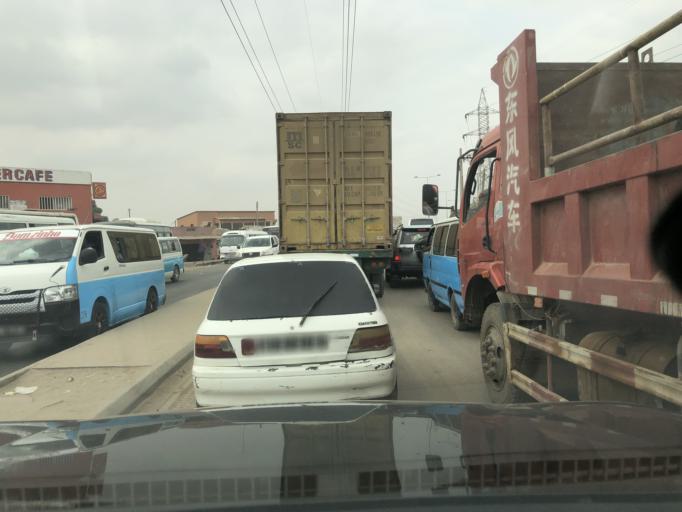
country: AO
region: Luanda
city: Luanda
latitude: -8.8169
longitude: 13.2785
